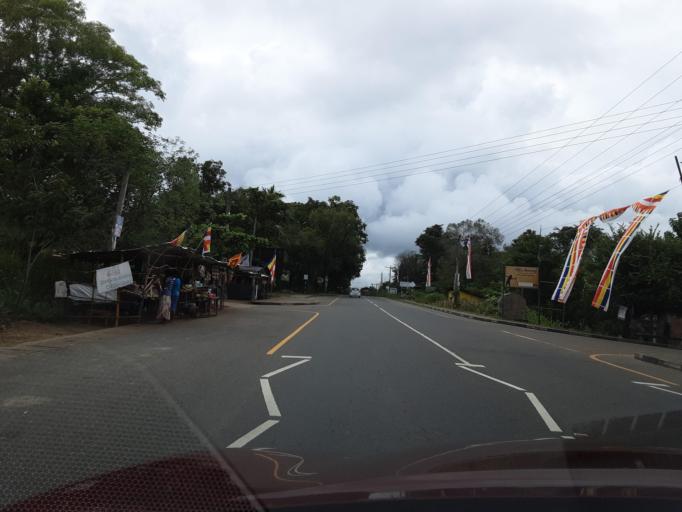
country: LK
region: Uva
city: Badulla
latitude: 7.3967
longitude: 81.1199
